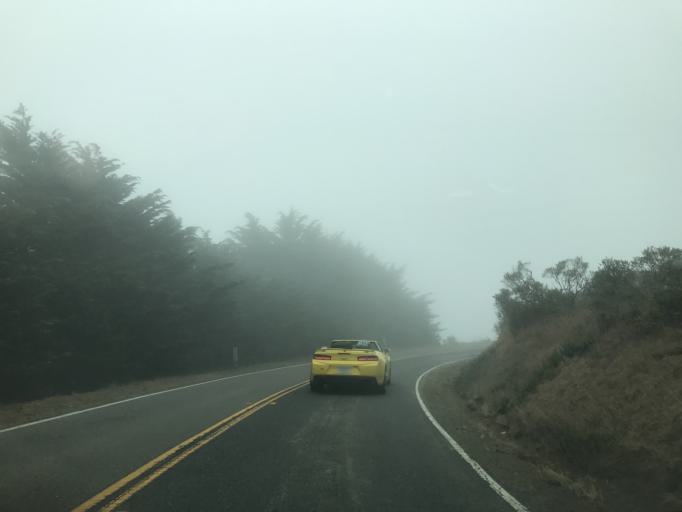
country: US
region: California
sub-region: Sonoma County
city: Monte Rio
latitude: 38.4772
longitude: -123.1585
